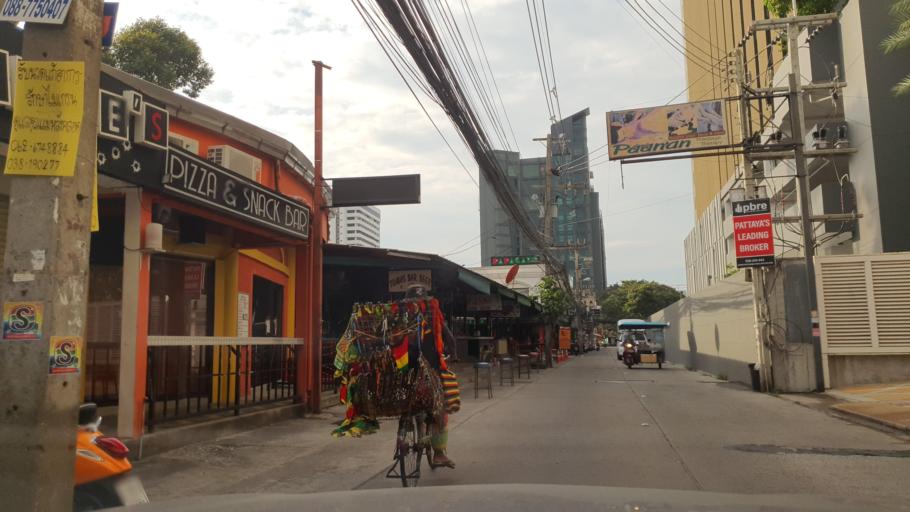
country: TH
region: Chon Buri
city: Phatthaya
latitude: 12.9301
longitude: 100.8831
